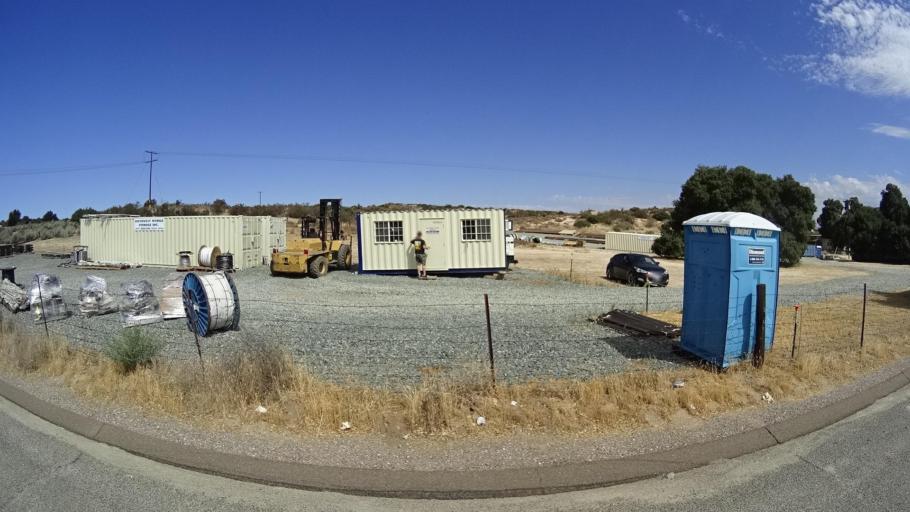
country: US
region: California
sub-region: San Diego County
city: Campo
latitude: 32.6742
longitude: -116.2907
